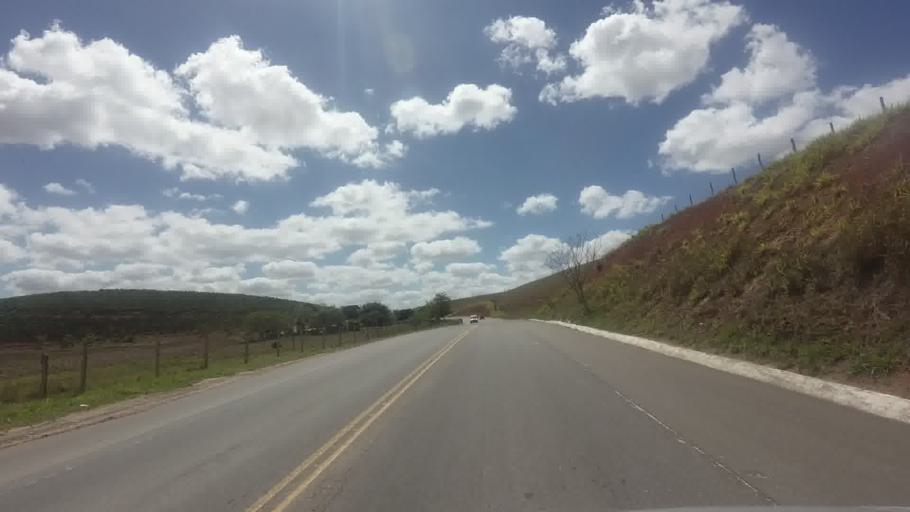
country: BR
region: Minas Gerais
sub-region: Recreio
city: Recreio
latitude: -21.6594
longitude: -42.3734
